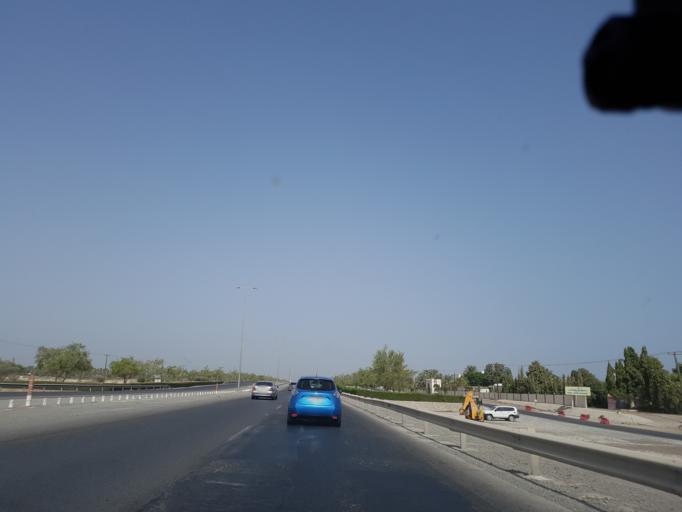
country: OM
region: Al Batinah
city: Barka'
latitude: 23.7297
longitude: 57.7068
